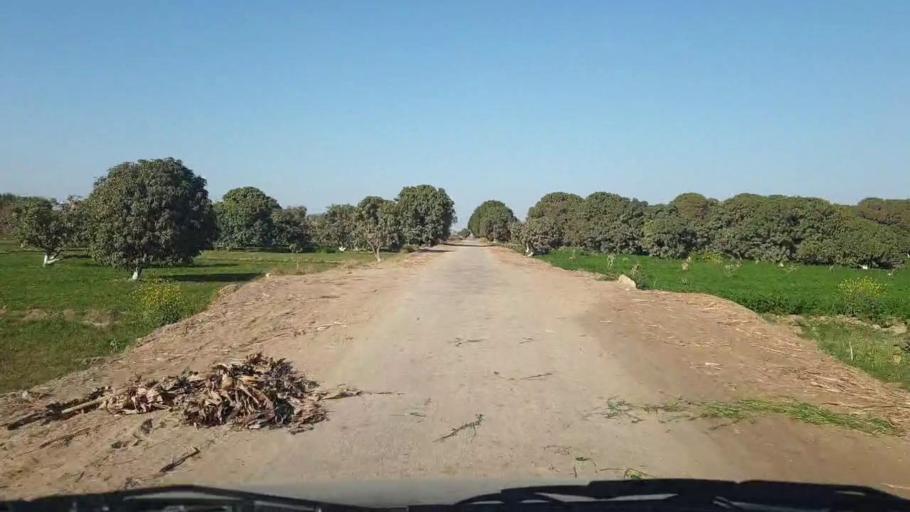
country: PK
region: Sindh
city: Samaro
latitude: 25.3593
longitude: 69.3012
